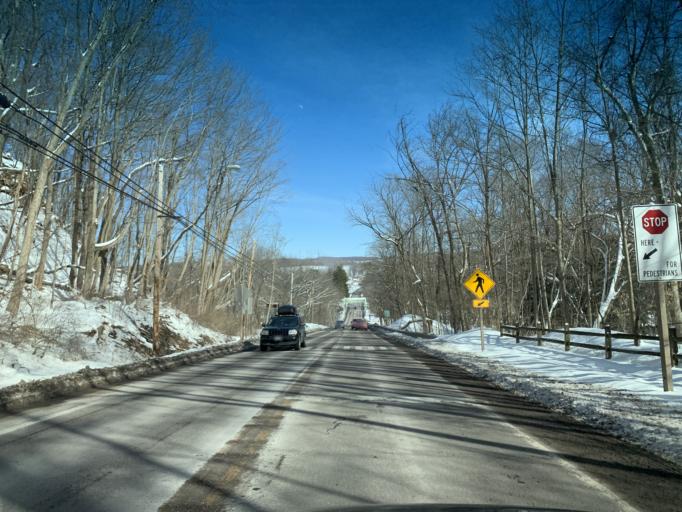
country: US
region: Pennsylvania
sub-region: Somerset County
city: Meyersdale
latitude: 39.6954
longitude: -79.1462
